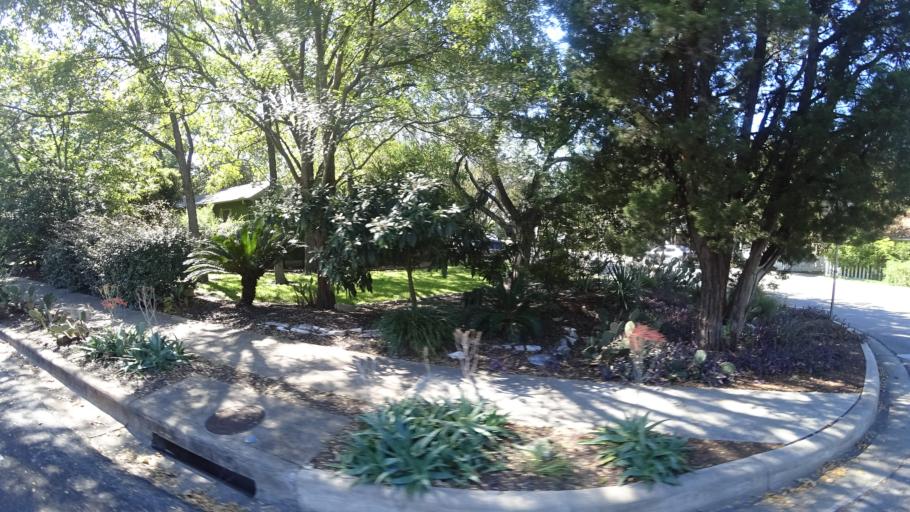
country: US
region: Texas
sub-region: Travis County
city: Rollingwood
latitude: 30.2945
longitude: -97.7660
